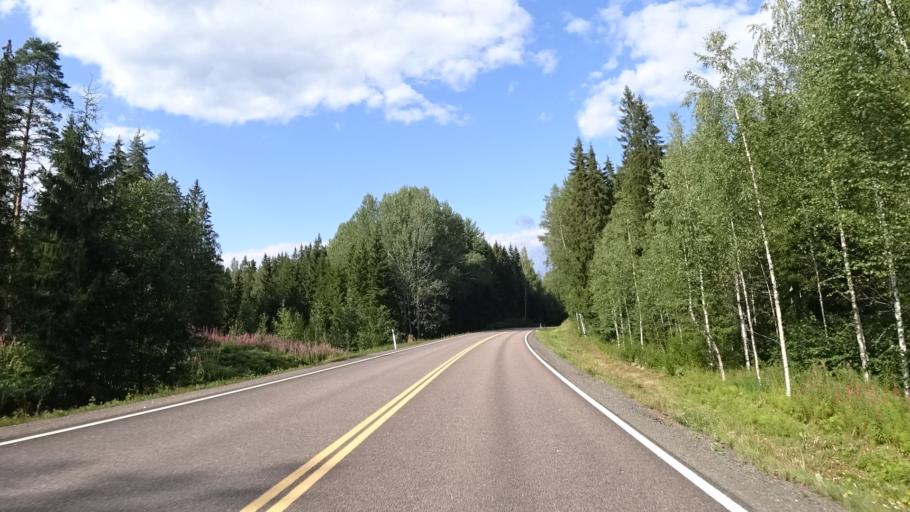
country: FI
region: Kymenlaakso
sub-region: Kotka-Hamina
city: Hamina
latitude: 60.6801
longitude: 27.2758
